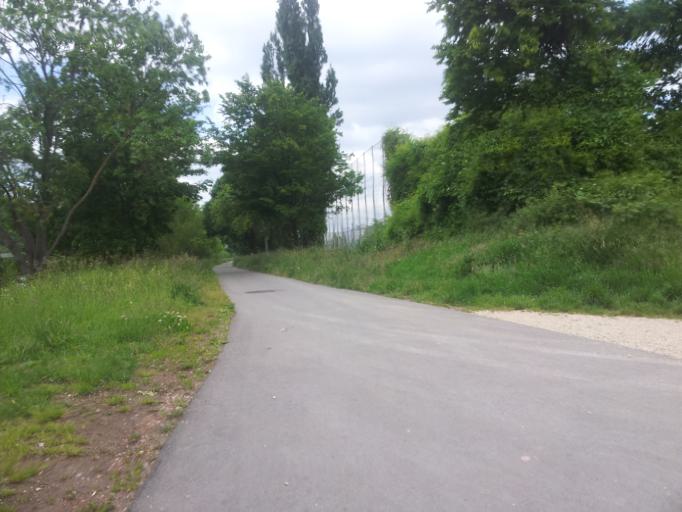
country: DE
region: Baden-Wuerttemberg
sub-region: Regierungsbezirk Stuttgart
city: Ostfildern
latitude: 48.7433
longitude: 9.2743
